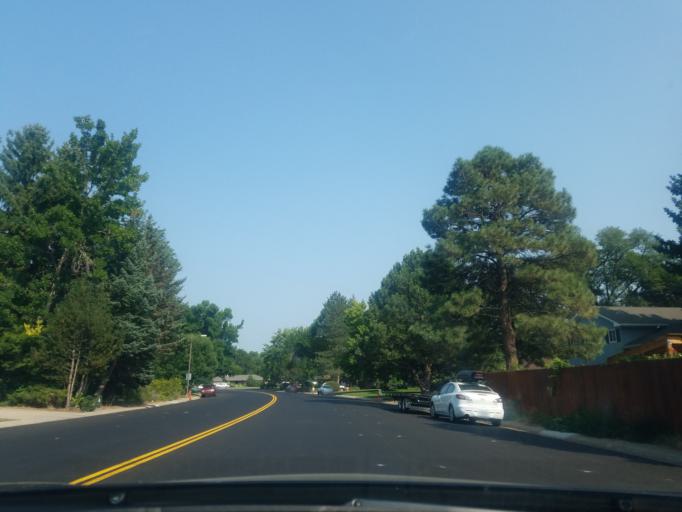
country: US
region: Colorado
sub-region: Larimer County
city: Fort Collins
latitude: 40.5697
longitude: -105.0600
